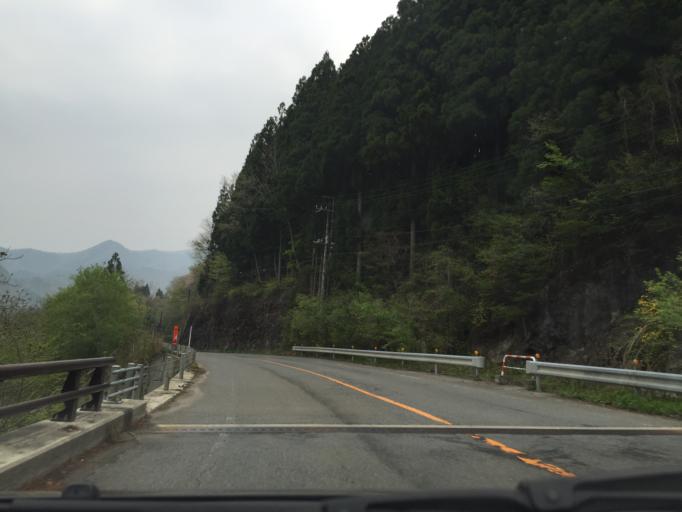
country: JP
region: Tochigi
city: Nikko
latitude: 36.9366
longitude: 139.6951
